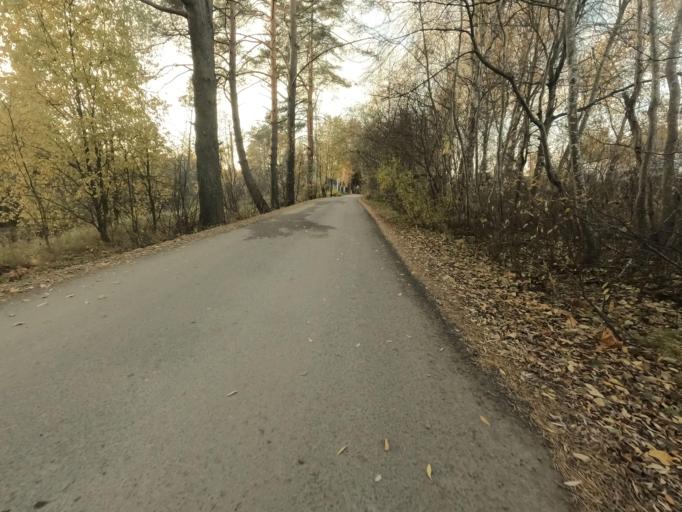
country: RU
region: St.-Petersburg
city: Beloostrov
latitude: 60.1617
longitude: 30.0030
